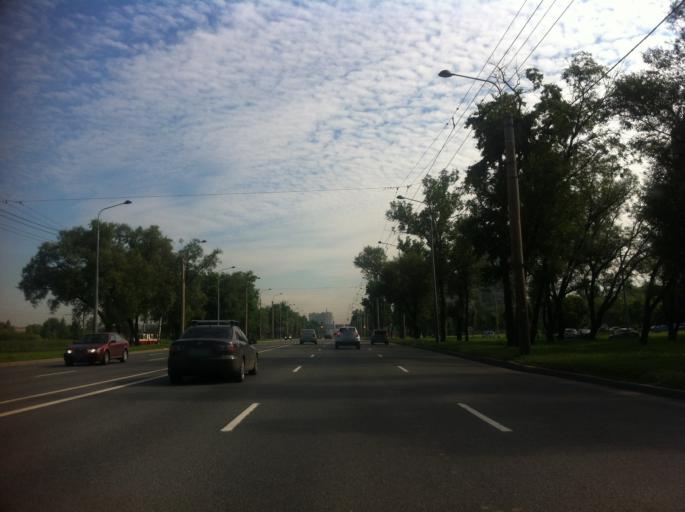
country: RU
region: St.-Petersburg
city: Uritsk
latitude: 59.8374
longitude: 30.2007
